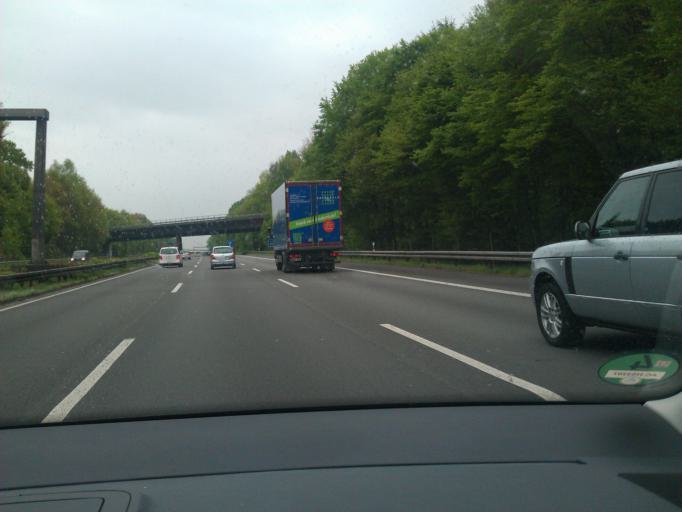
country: DE
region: North Rhine-Westphalia
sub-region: Regierungsbezirk Koln
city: Siegburg
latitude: 50.8162
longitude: 7.2115
